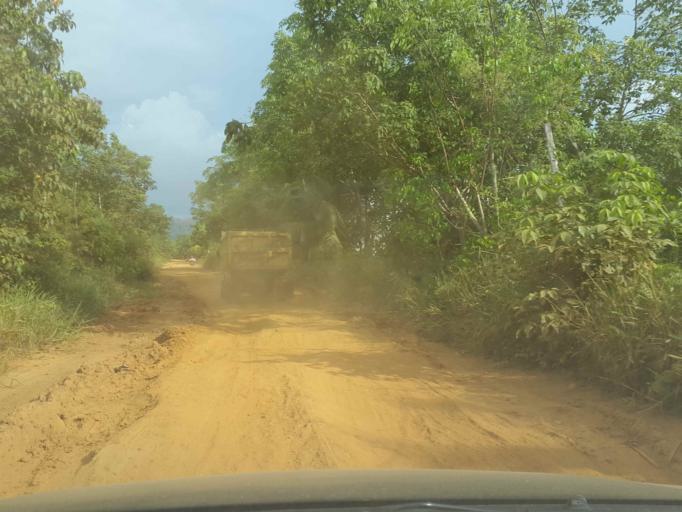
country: ID
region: West Kalimantan
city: Pemangkat
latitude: 1.7818
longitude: 109.3416
